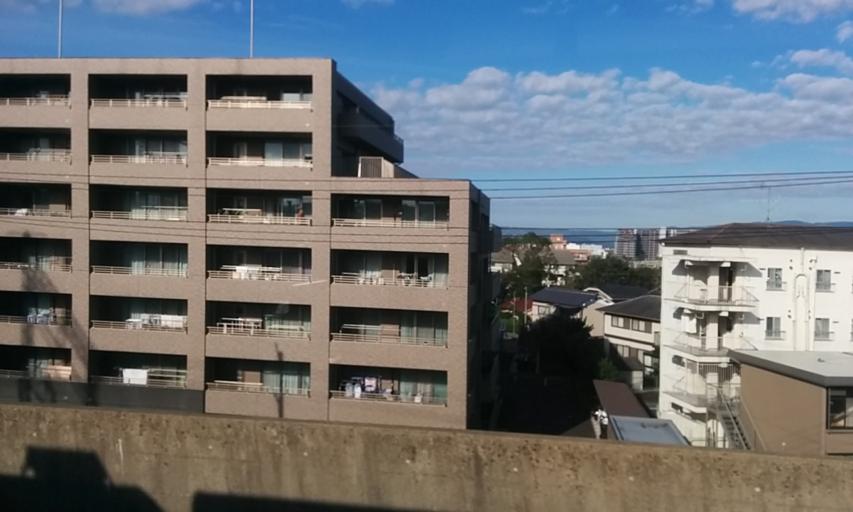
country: JP
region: Kyoto
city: Uji
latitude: 34.8712
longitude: 135.7763
